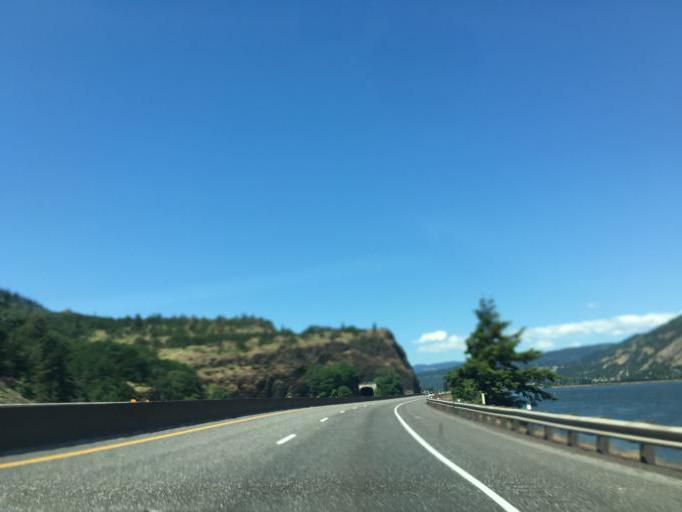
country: US
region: Washington
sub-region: Klickitat County
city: White Salmon
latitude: 45.6891
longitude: -121.4370
